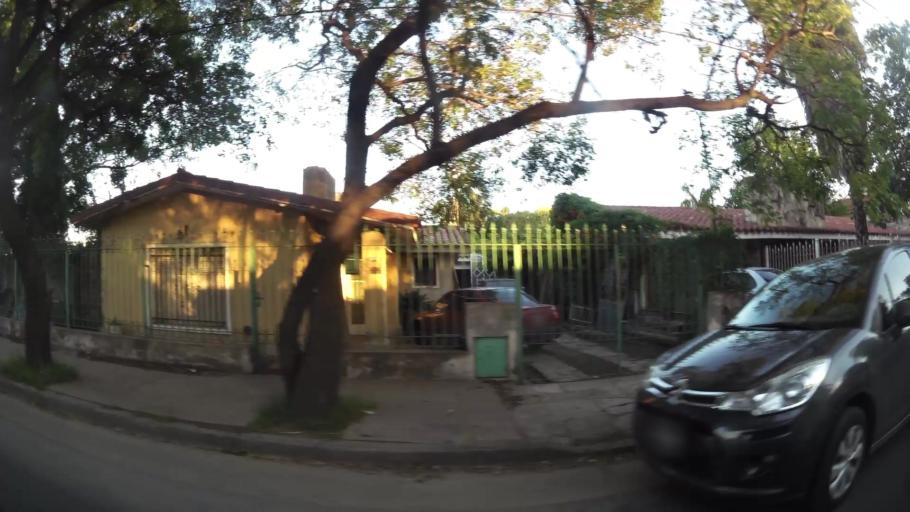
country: AR
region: Cordoba
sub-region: Departamento de Capital
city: Cordoba
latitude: -31.3749
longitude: -64.2225
